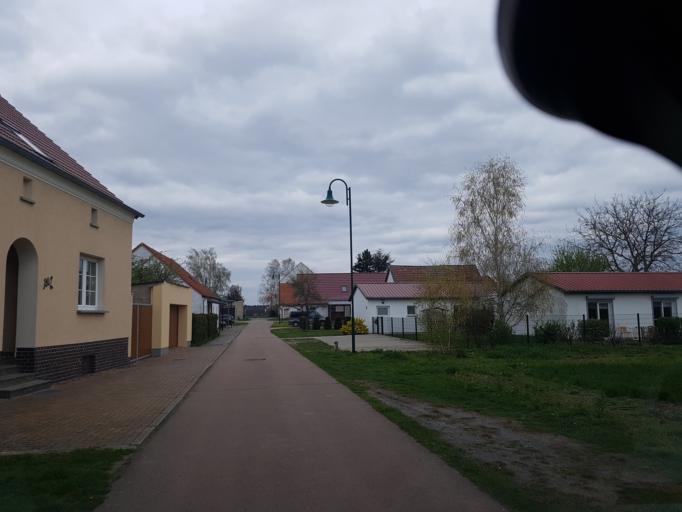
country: DE
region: Brandenburg
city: Juterbog
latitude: 51.9151
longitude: 13.0978
